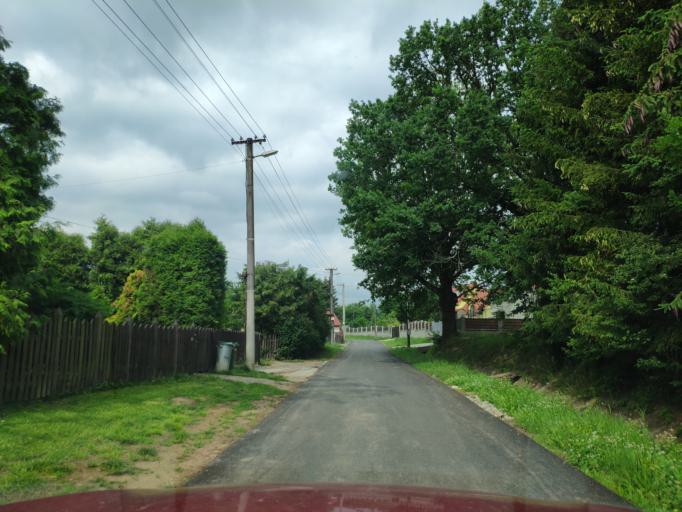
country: SK
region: Kosicky
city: Kosice
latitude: 48.8014
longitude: 21.3011
